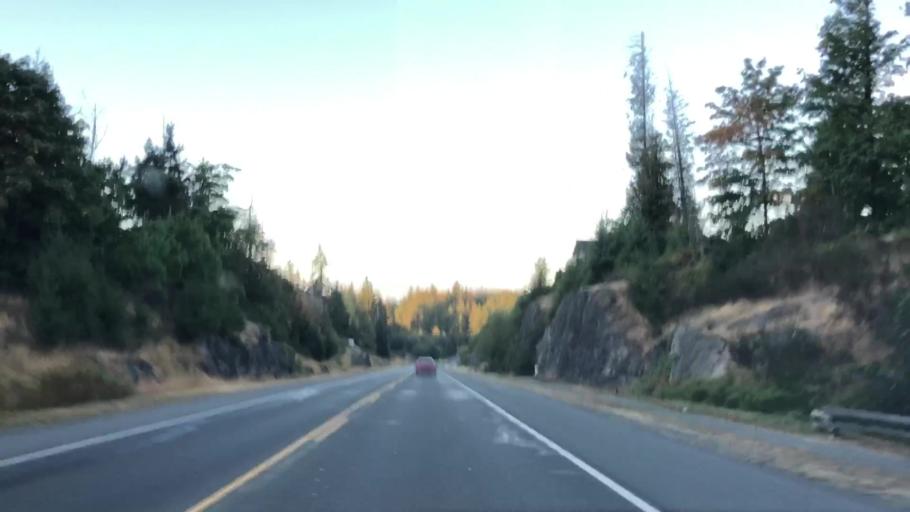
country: CA
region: British Columbia
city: Colwood
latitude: 48.4124
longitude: -123.5059
